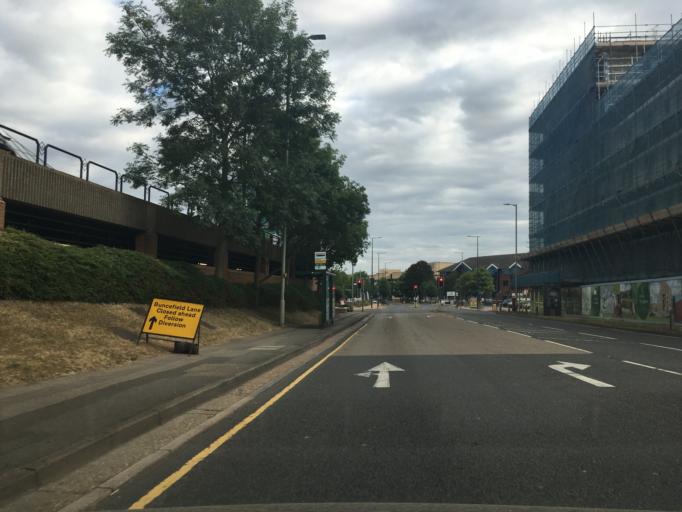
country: GB
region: England
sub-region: Hertfordshire
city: Hemel Hempstead
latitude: 51.7610
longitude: -0.4385
